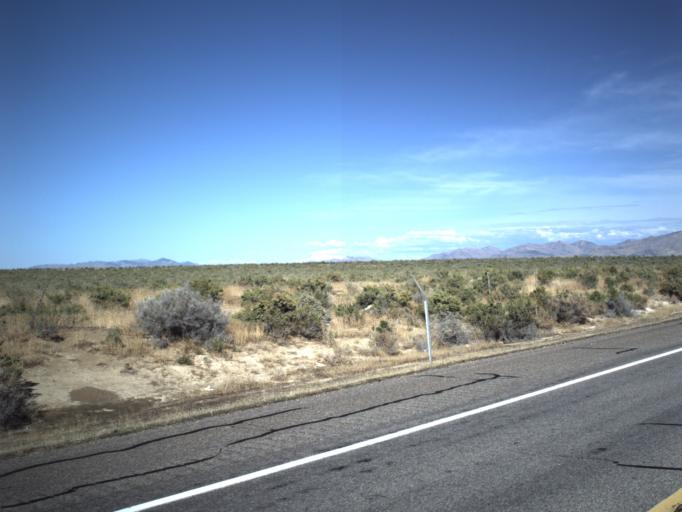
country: US
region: Utah
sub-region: Millard County
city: Delta
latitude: 39.3533
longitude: -112.5039
